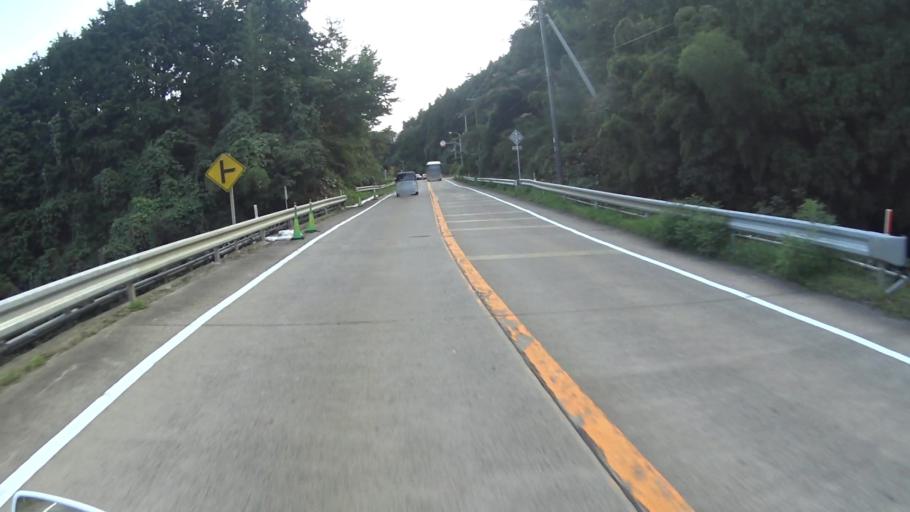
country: JP
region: Kyoto
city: Miyazu
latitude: 35.4580
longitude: 135.0753
